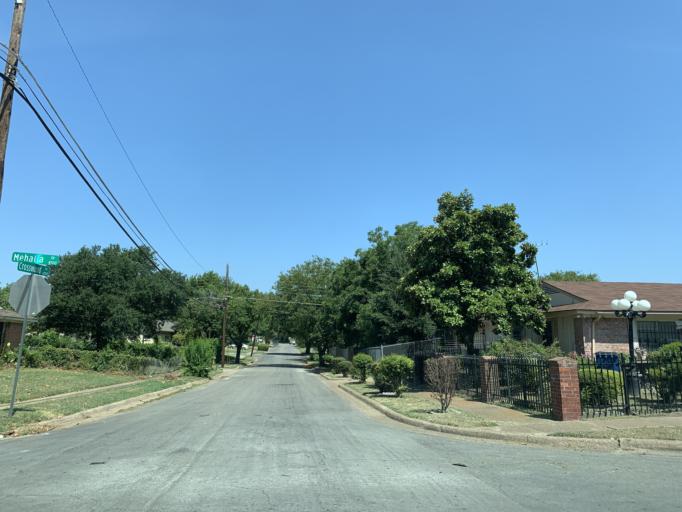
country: US
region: Texas
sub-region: Dallas County
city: Hutchins
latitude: 32.6740
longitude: -96.7511
